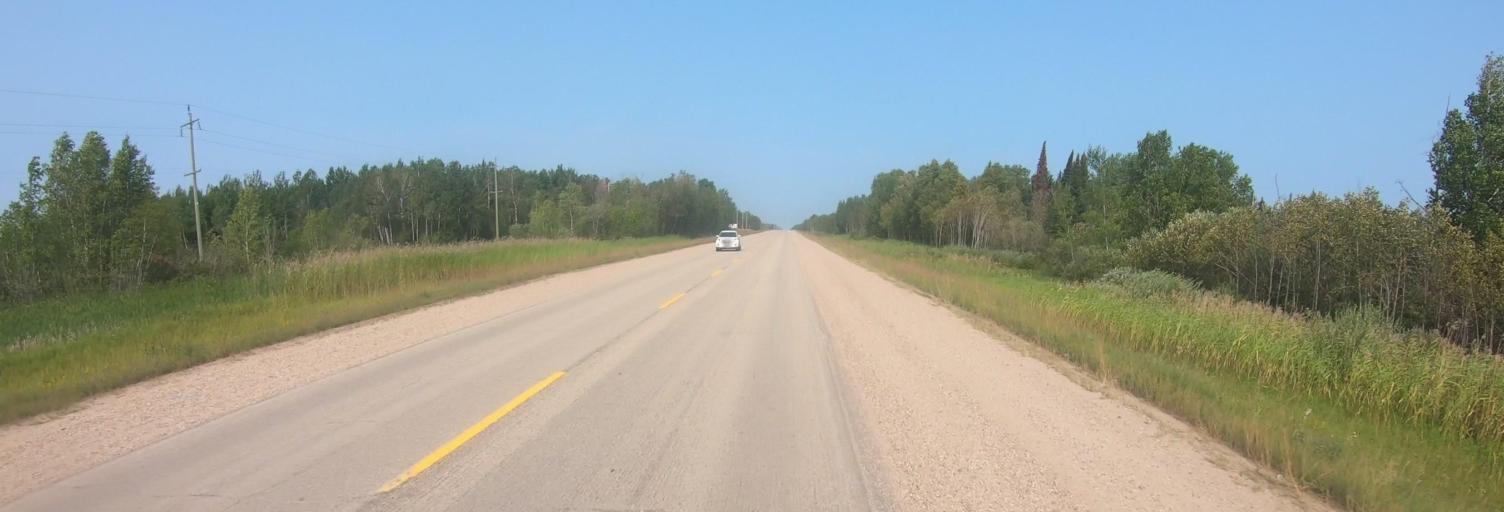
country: US
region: Minnesota
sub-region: Roseau County
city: Roseau
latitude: 49.0438
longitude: -95.7848
